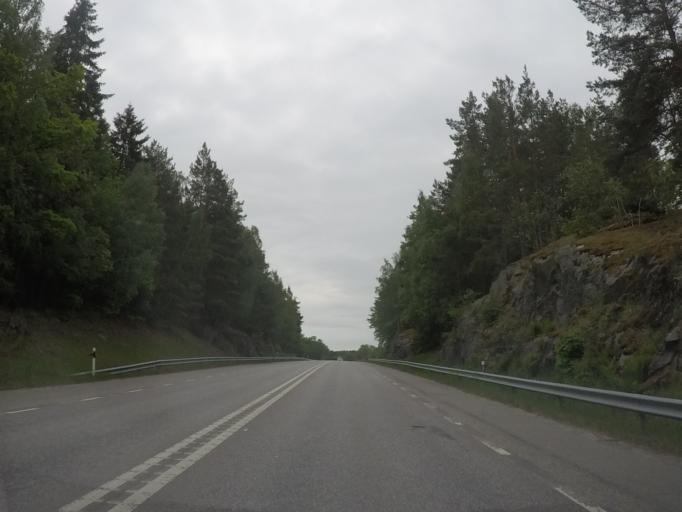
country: SE
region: Soedermanland
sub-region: Nykopings Kommun
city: Stigtomta
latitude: 58.8228
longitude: 16.7583
